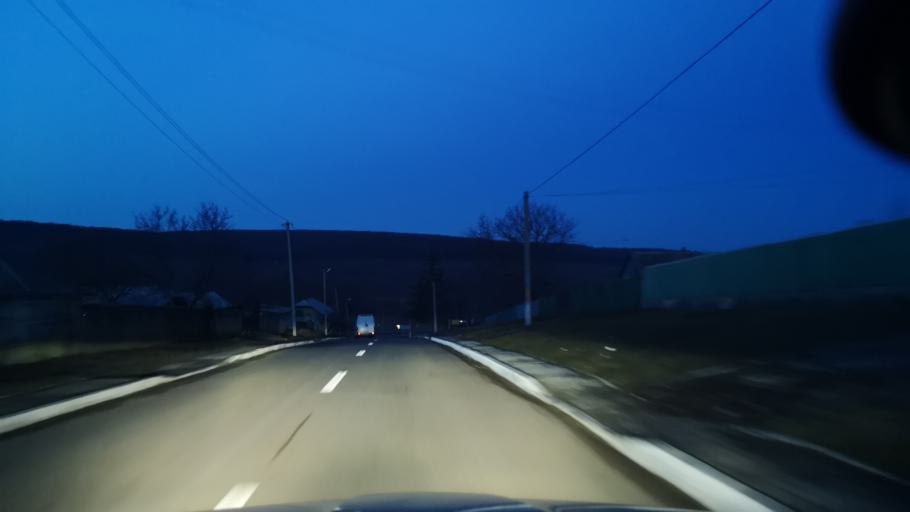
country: MD
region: Orhei
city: Orhei
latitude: 47.3383
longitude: 28.6574
